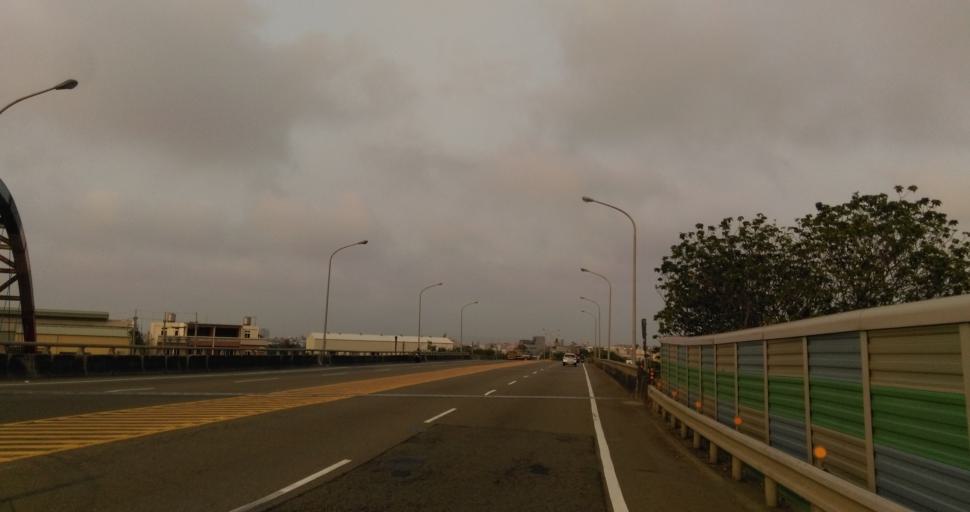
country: TW
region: Taiwan
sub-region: Hsinchu
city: Hsinchu
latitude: 24.8090
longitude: 120.9189
